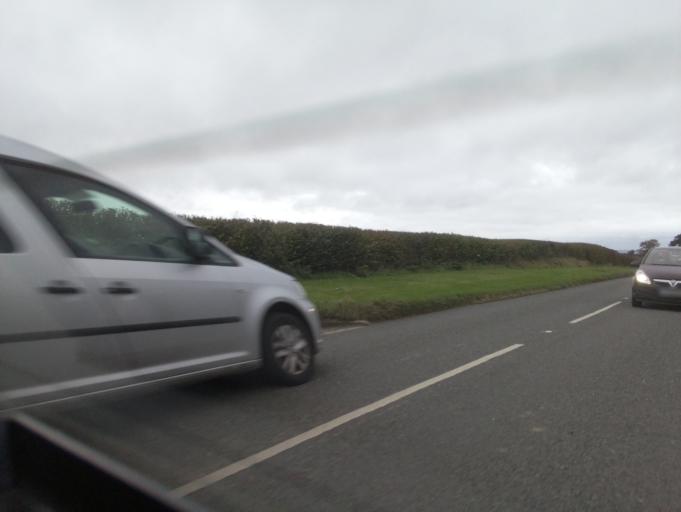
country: GB
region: England
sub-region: Dorset
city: Sherborne
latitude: 50.9749
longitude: -2.5587
